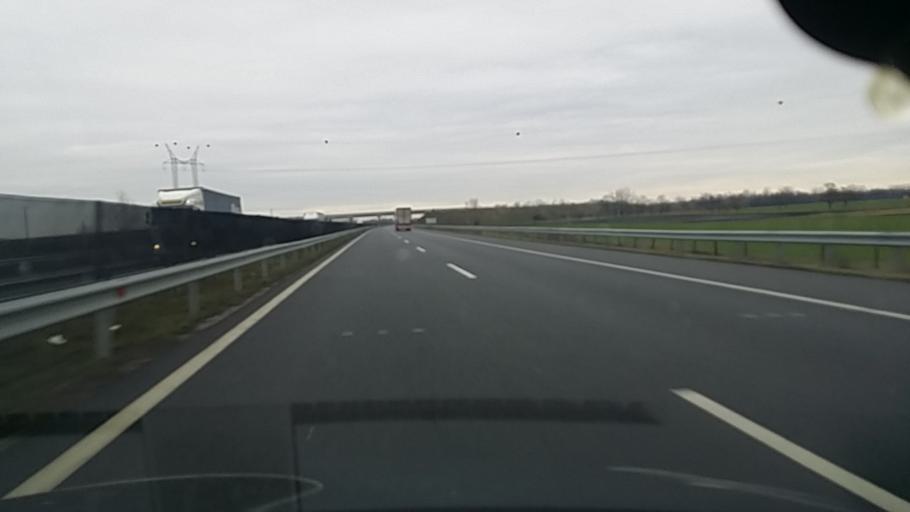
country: HU
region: Hajdu-Bihar
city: Hajdunanas
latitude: 47.8592
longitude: 21.3598
